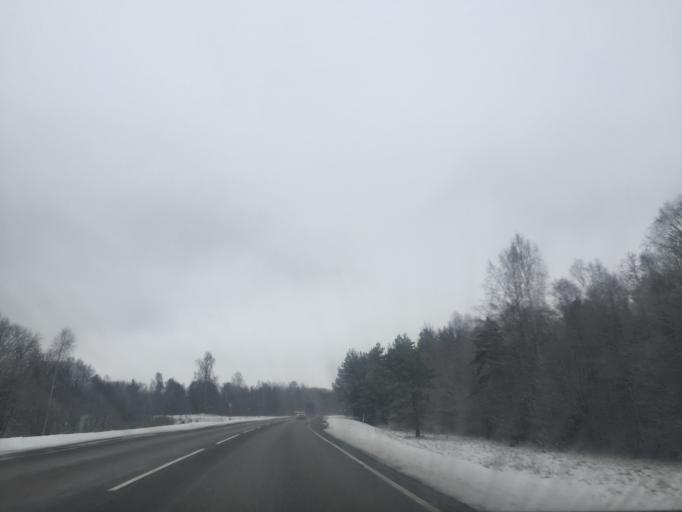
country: EE
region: Laeaene
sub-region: Lihula vald
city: Lihula
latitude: 58.6385
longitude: 23.6911
